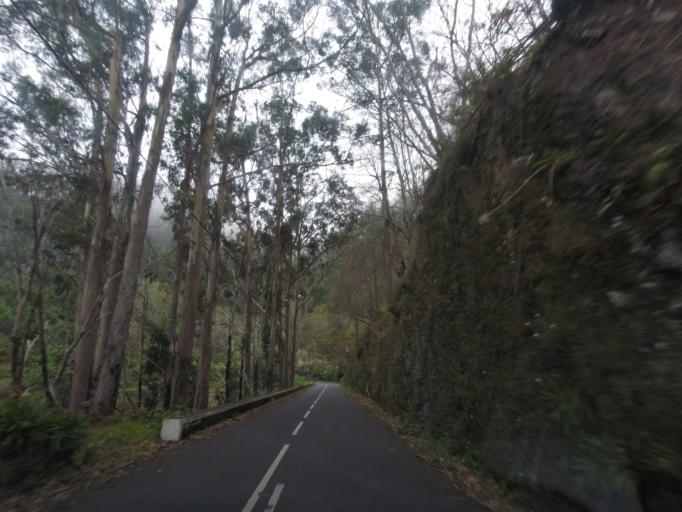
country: PT
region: Madeira
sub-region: Funchal
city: Nossa Senhora do Monte
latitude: 32.6817
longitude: -16.8837
